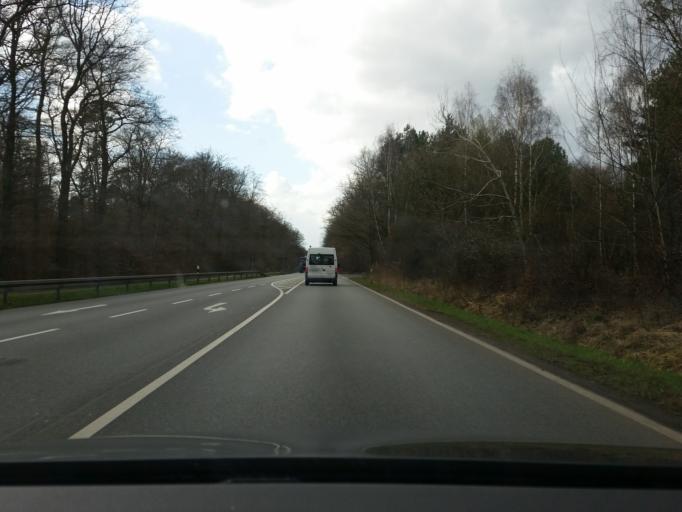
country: DE
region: Hesse
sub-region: Regierungsbezirk Giessen
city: Giessen
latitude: 50.5706
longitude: 8.7254
